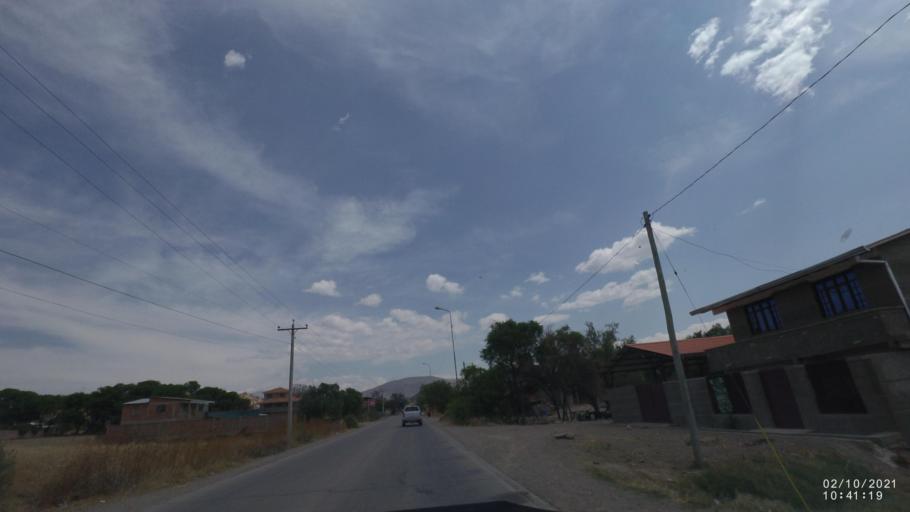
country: BO
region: Cochabamba
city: Capinota
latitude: -17.6149
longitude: -66.2903
